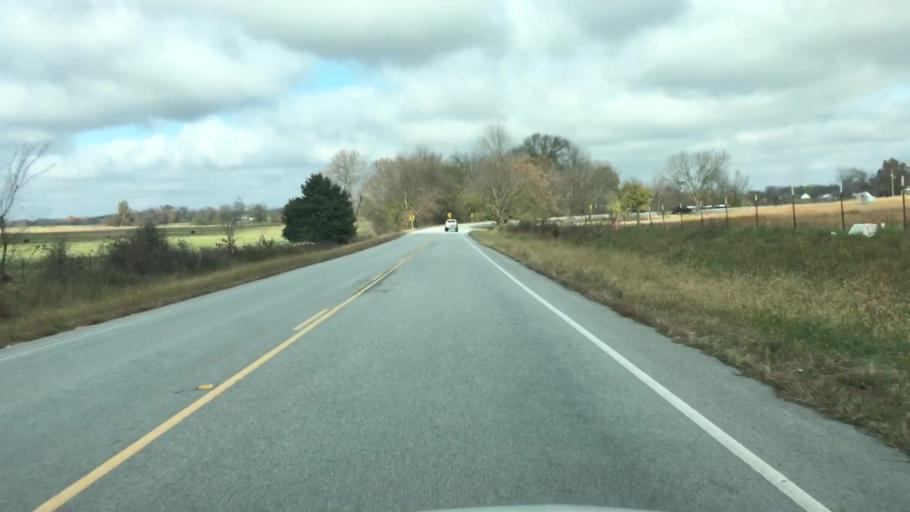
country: US
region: Arkansas
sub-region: Benton County
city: Centerton
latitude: 36.2846
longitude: -94.3501
